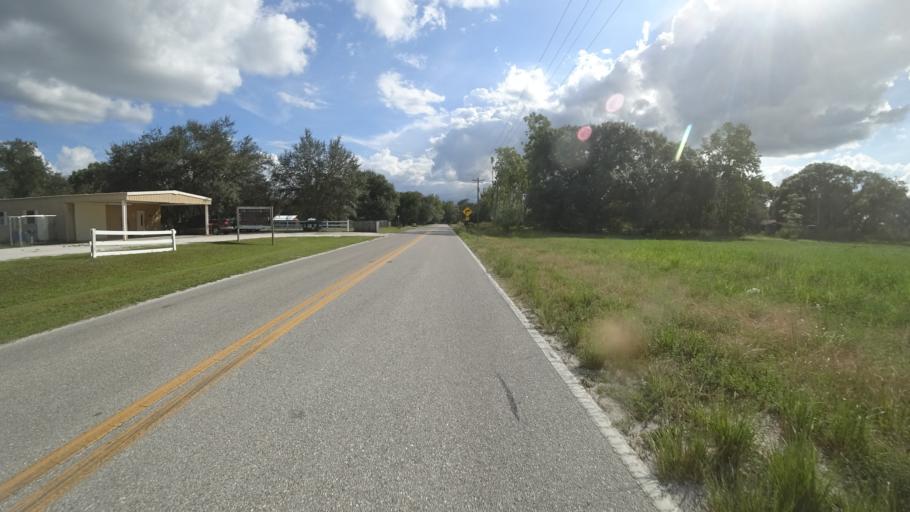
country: US
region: Florida
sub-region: Sarasota County
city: Lake Sarasota
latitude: 27.3473
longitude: -82.1626
